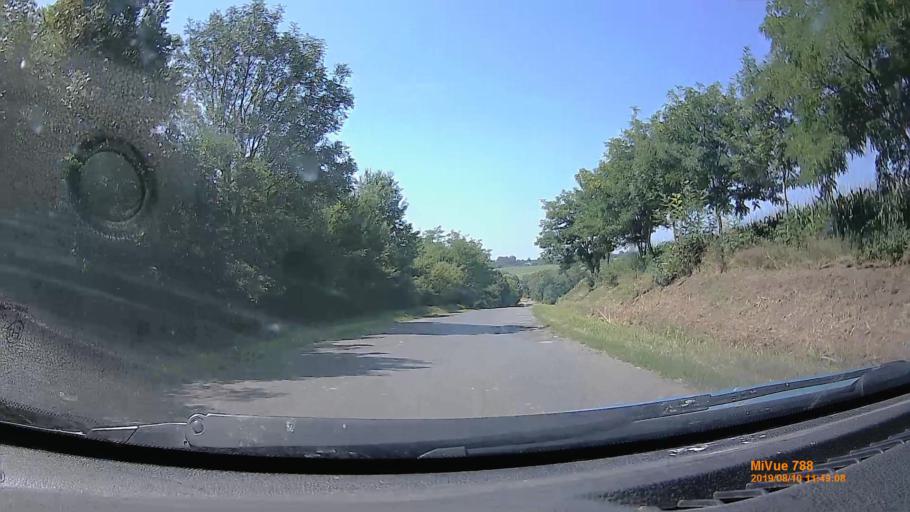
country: HU
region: Somogy
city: Somogyvar
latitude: 46.4992
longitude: 17.7325
